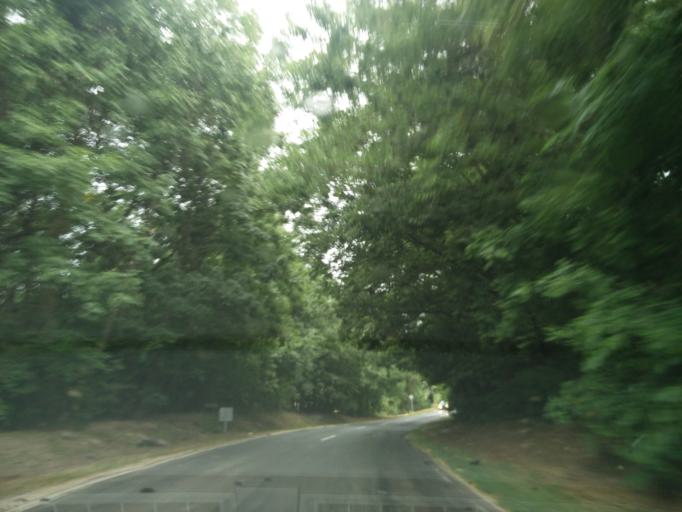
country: HU
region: Fejer
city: Bicske
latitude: 47.4312
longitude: 18.6349
